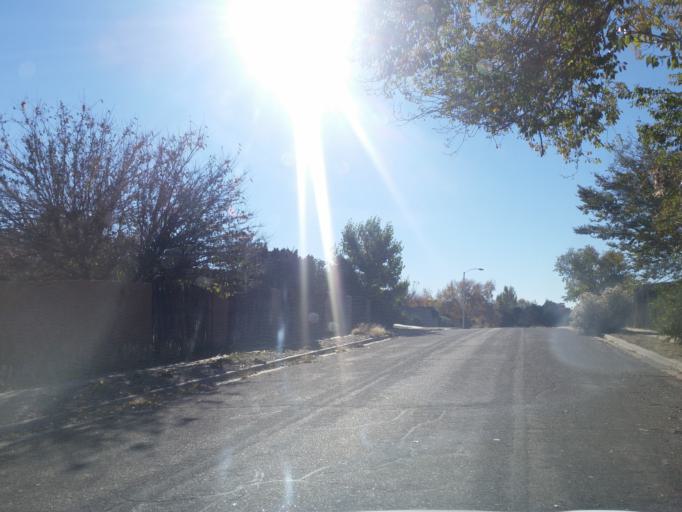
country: US
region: New Mexico
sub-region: Santa Fe County
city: Santa Fe
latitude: 35.6488
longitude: -105.9323
